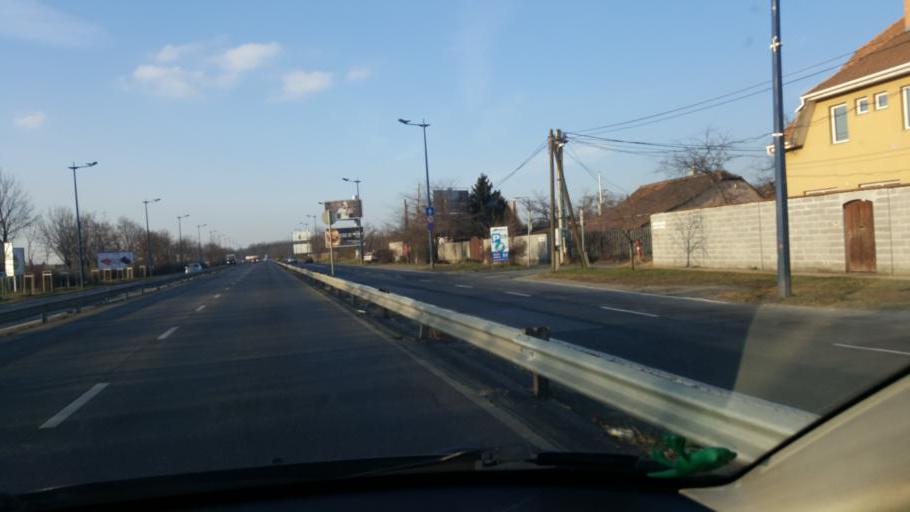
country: HU
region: Budapest
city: Budapest XVIII. keruelet
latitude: 47.4475
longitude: 19.2075
